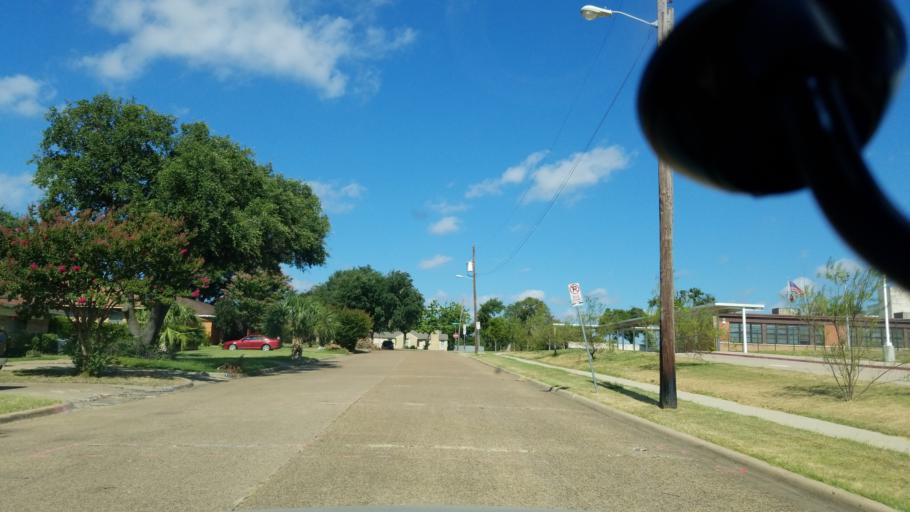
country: US
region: Texas
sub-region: Dallas County
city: Cockrell Hill
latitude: 32.6773
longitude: -96.8133
